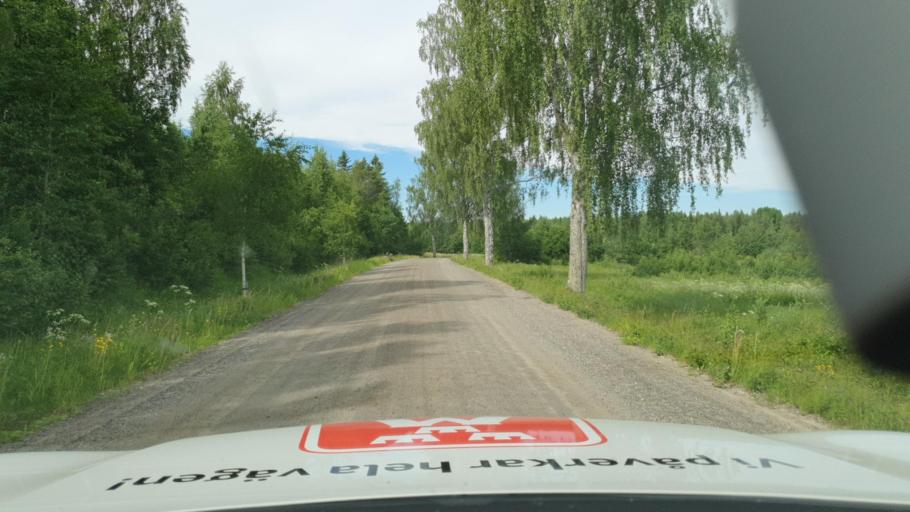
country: SE
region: Vaesterbotten
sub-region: Skelleftea Kommun
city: Burtraesk
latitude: 64.4795
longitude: 20.4777
